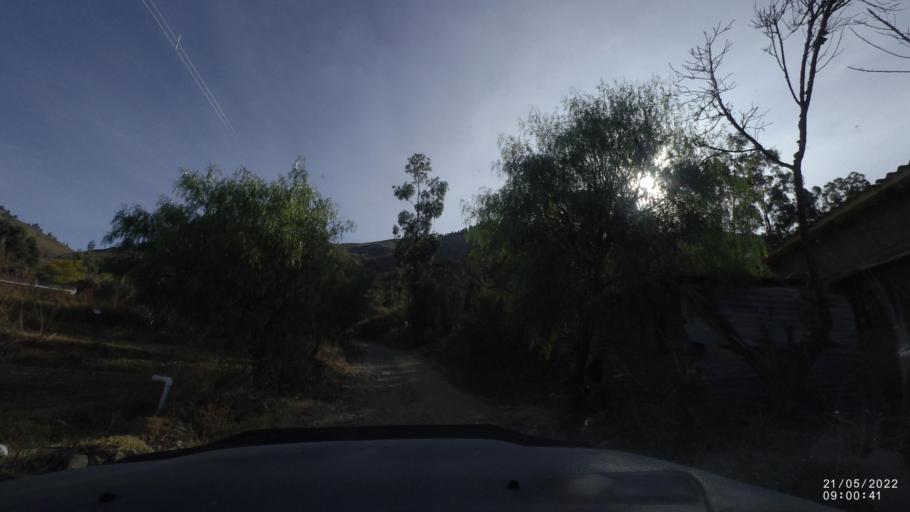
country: BO
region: Cochabamba
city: Cochabamba
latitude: -17.3765
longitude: -66.0348
